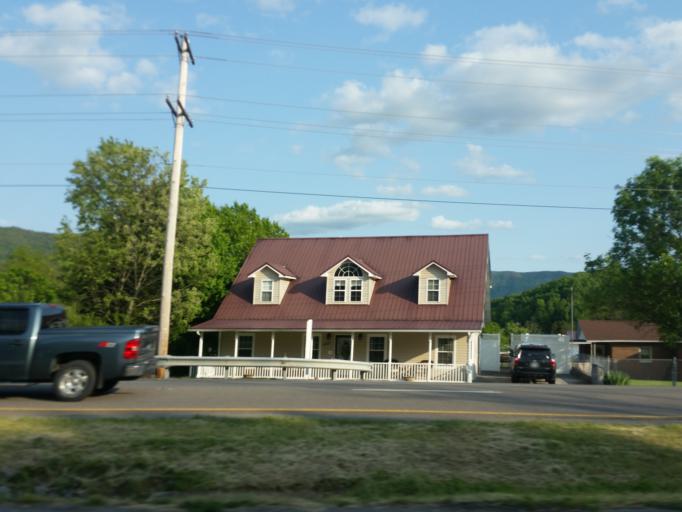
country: US
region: Virginia
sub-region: Tazewell County
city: Claypool Hill
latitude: 37.0577
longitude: -81.7633
